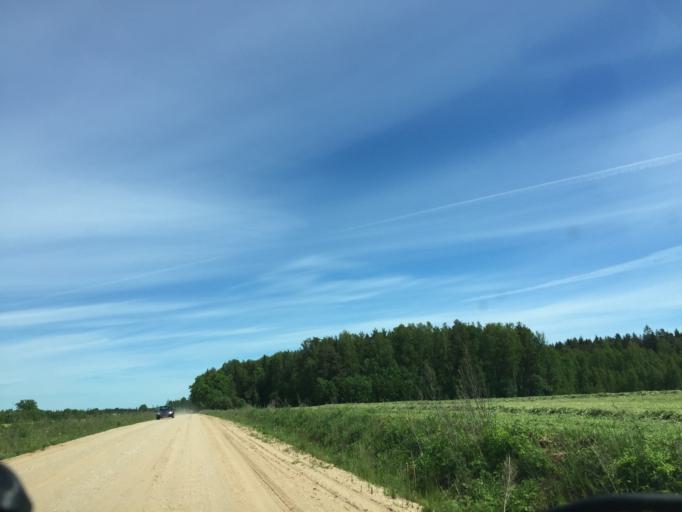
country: LV
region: Cesu Rajons
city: Cesis
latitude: 57.4354
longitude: 25.2059
